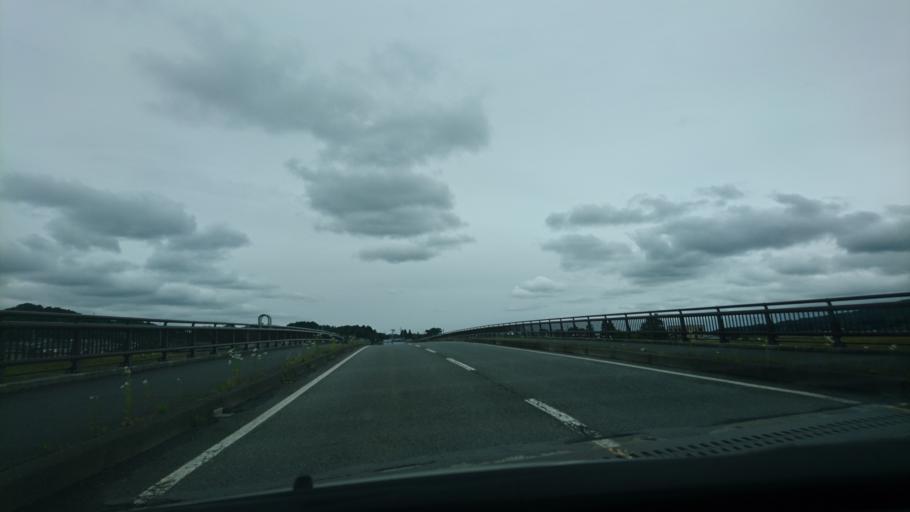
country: JP
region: Iwate
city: Ichinoseki
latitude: 38.9842
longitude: 141.1164
